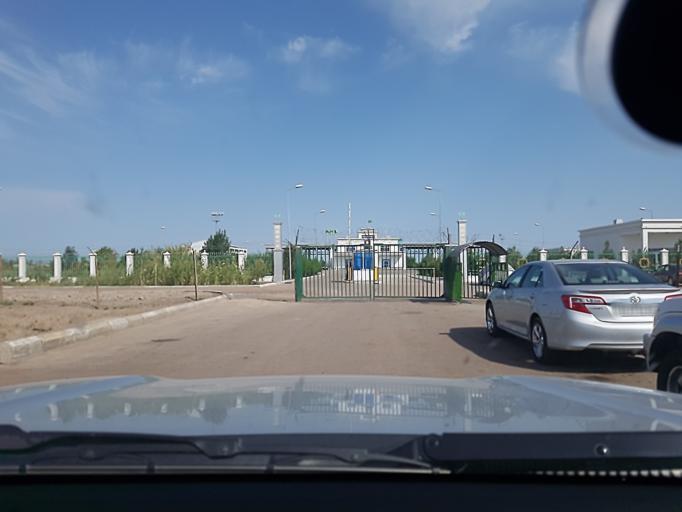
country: TM
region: Dasoguz
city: Dasoguz
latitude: 41.7741
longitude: 60.0570
